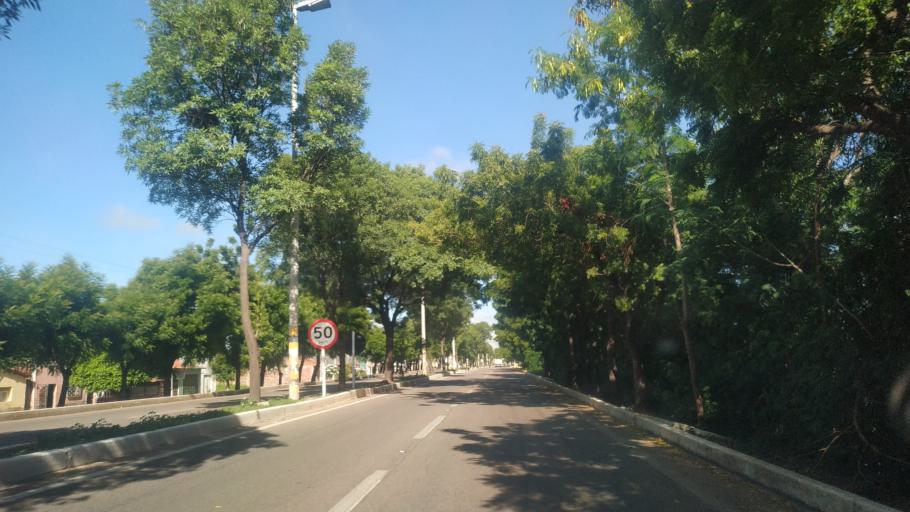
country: BR
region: Rio Grande do Norte
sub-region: Mossoro
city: Mossoro
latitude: -5.1919
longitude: -37.3649
